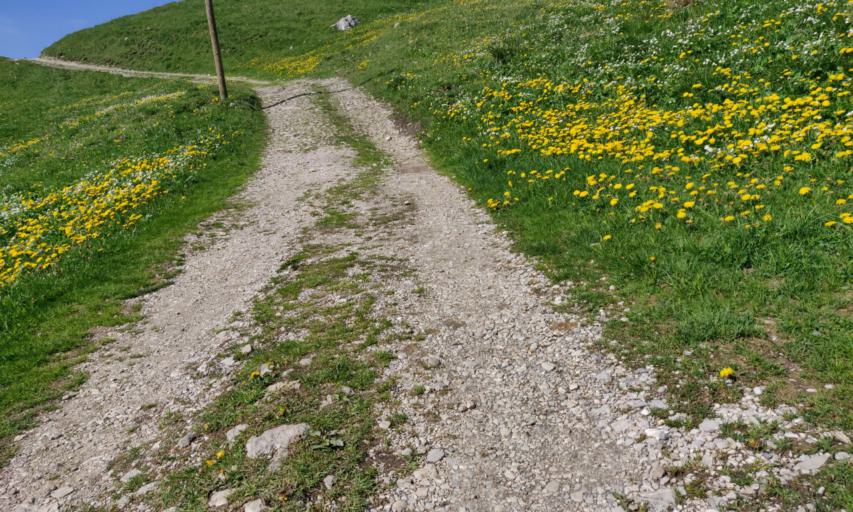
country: CH
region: Fribourg
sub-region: Gruyere District
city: Vuadens
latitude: 46.5515
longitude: 7.0021
